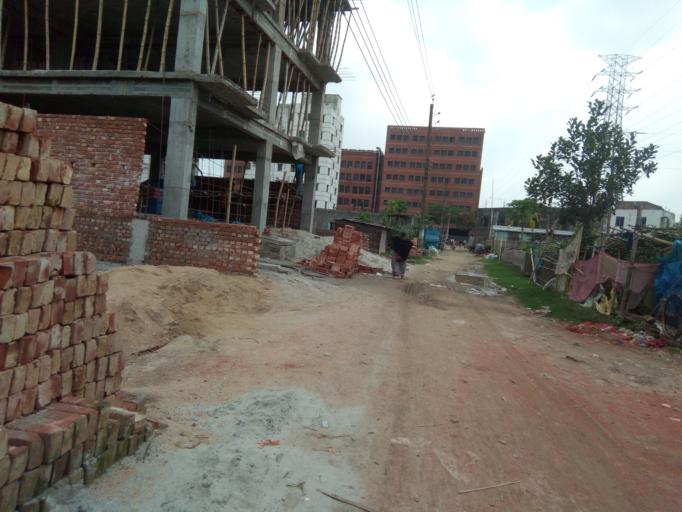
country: BD
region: Dhaka
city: Paltan
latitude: 23.7682
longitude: 90.4273
